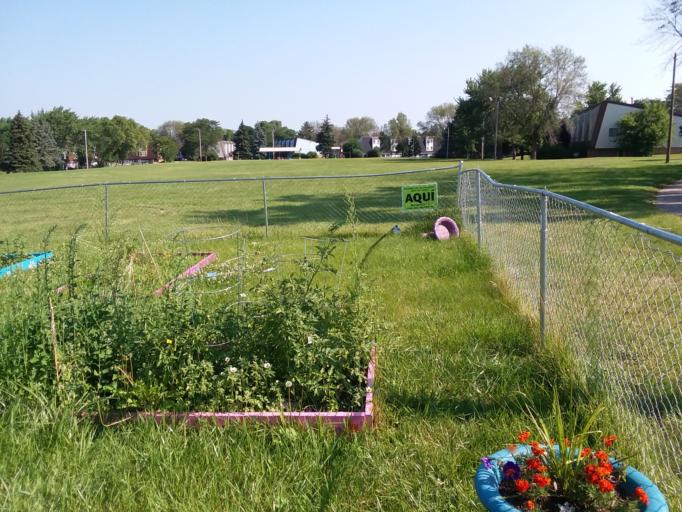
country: US
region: Wisconsin
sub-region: Milwaukee County
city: Brown Deer
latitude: 43.1798
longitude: -88.0263
